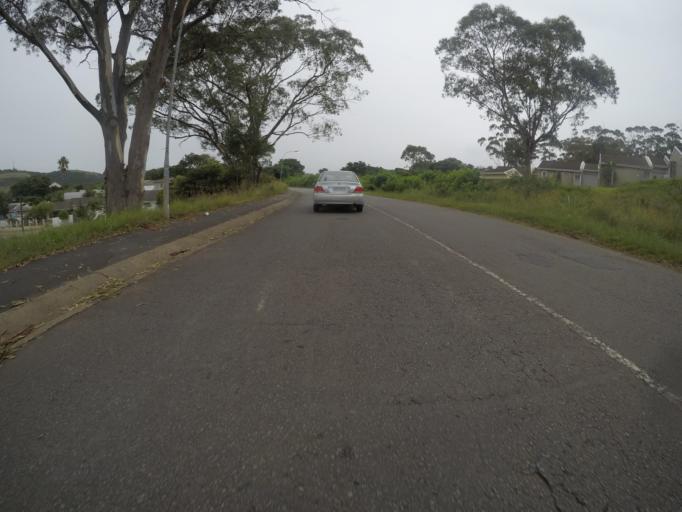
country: ZA
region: Eastern Cape
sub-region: Buffalo City Metropolitan Municipality
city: East London
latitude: -32.9590
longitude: 27.9149
